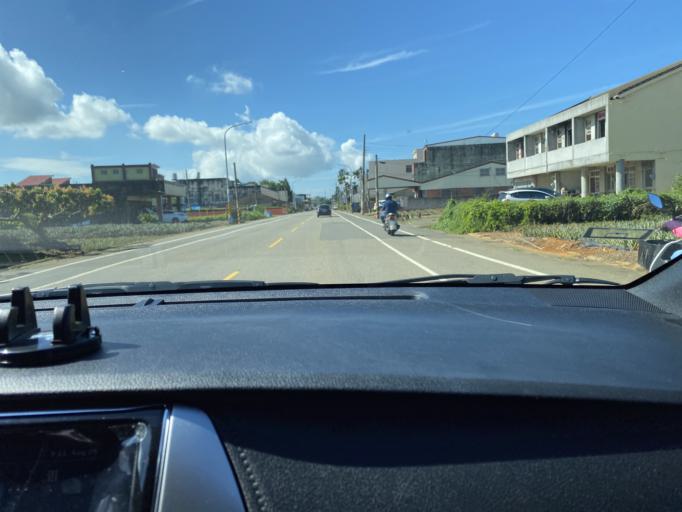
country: TW
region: Taiwan
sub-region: Nantou
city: Nantou
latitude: 23.9180
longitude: 120.6375
